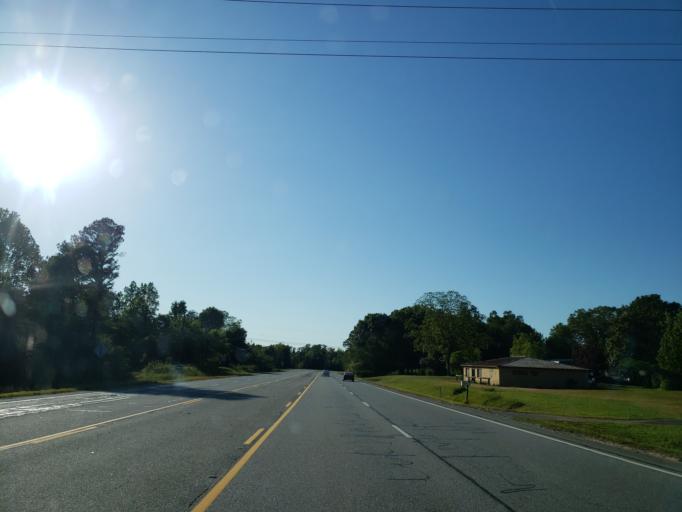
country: US
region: Georgia
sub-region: Haralson County
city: Buchanan
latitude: 33.8961
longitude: -85.2287
